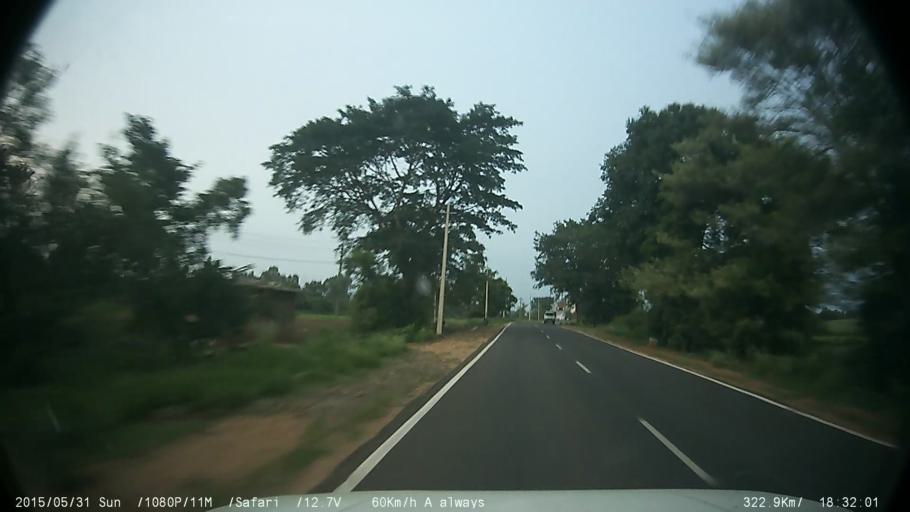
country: IN
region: Karnataka
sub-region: Mysore
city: Nanjangud
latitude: 12.1308
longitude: 76.7463
